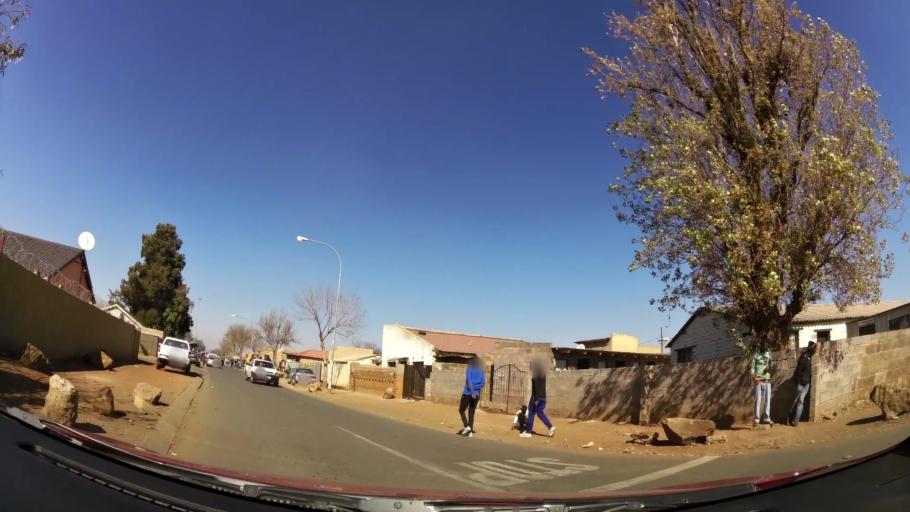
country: ZA
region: Gauteng
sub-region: City of Johannesburg Metropolitan Municipality
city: Soweto
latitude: -26.2394
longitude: 27.8375
